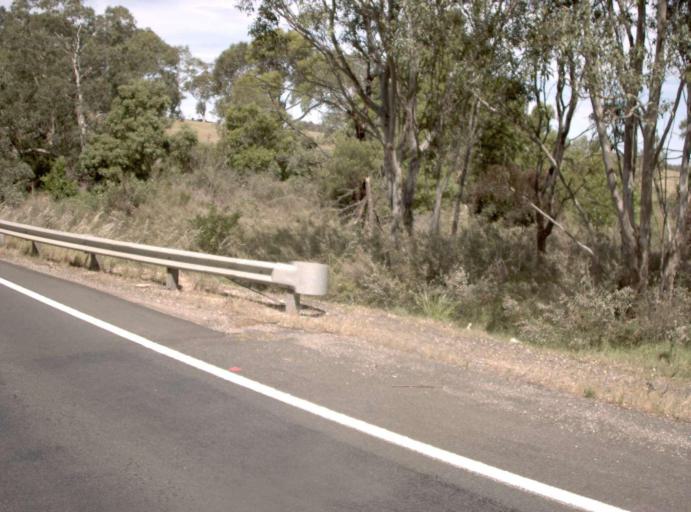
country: AU
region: Victoria
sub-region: East Gippsland
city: Bairnsdale
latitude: -37.9004
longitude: 147.3559
